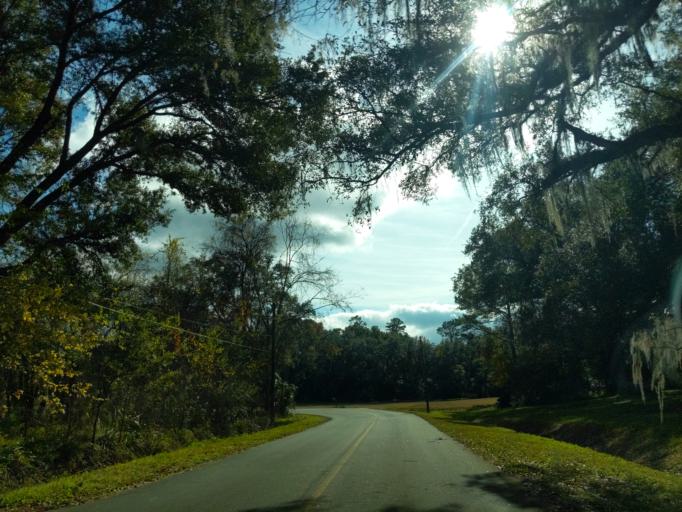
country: US
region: Florida
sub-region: Leon County
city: Tallahassee
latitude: 30.4726
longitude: -84.2051
